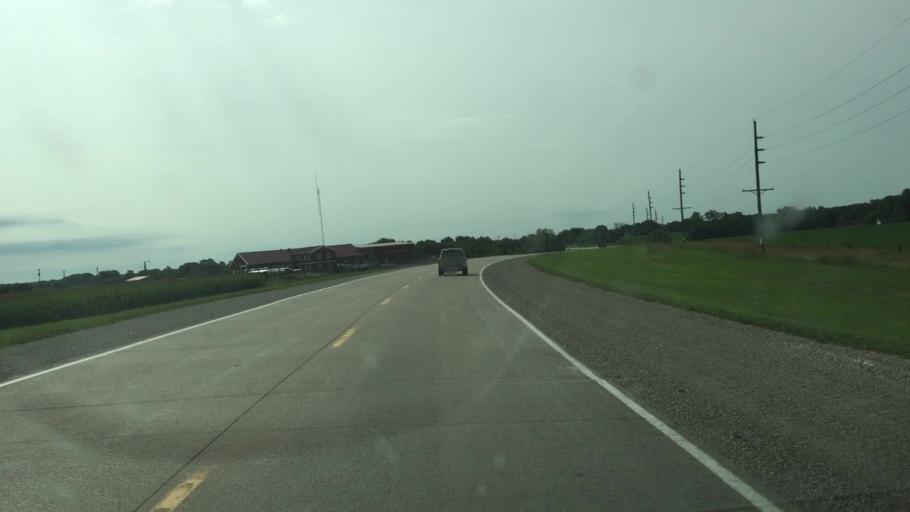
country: US
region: Illinois
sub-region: Hancock County
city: Nauvoo
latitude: 40.6377
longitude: -91.5207
